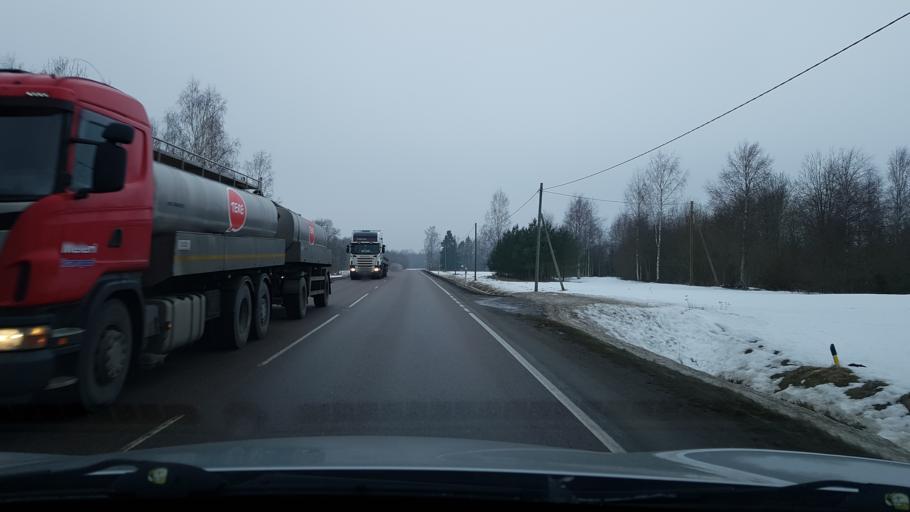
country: EE
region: Jogevamaa
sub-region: Poltsamaa linn
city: Poltsamaa
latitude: 58.4181
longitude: 26.0286
